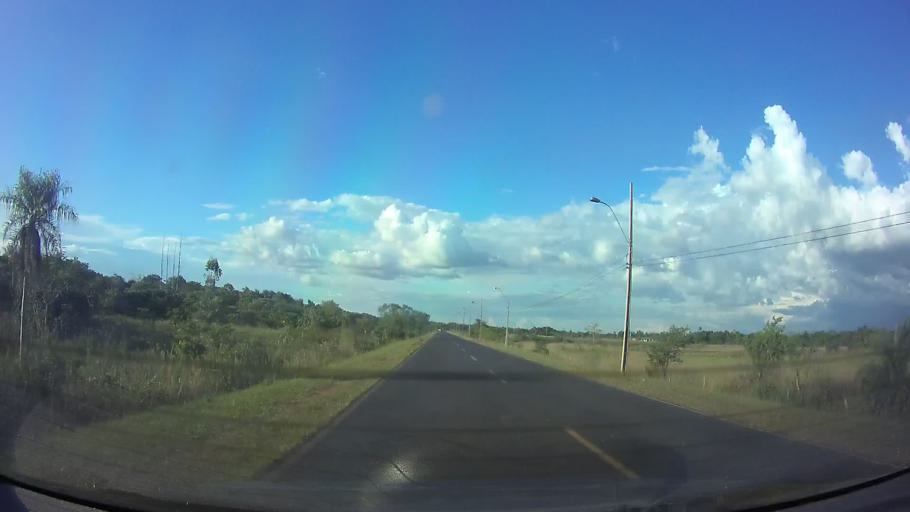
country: PY
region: Cordillera
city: Emboscada
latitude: -25.1495
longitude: -57.2607
